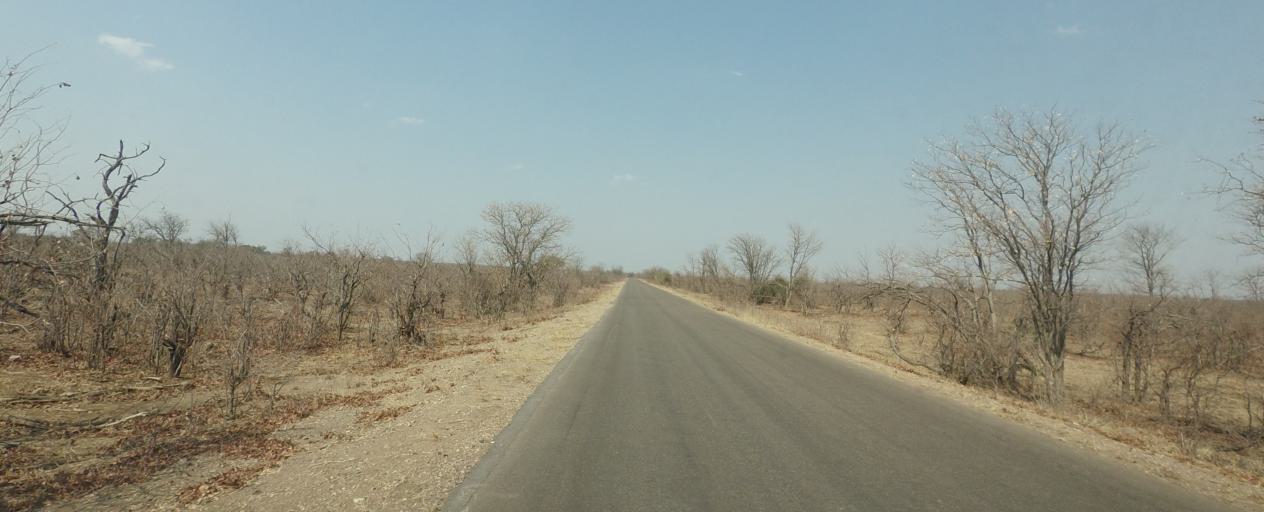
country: ZA
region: Limpopo
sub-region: Mopani District Municipality
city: Giyani
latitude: -23.1678
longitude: 31.3396
